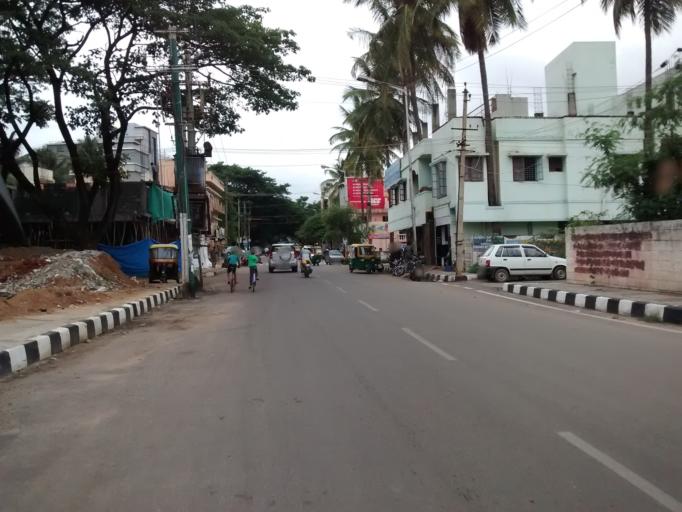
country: IN
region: Karnataka
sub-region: Bangalore Urban
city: Yelahanka
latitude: 13.0422
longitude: 77.5827
